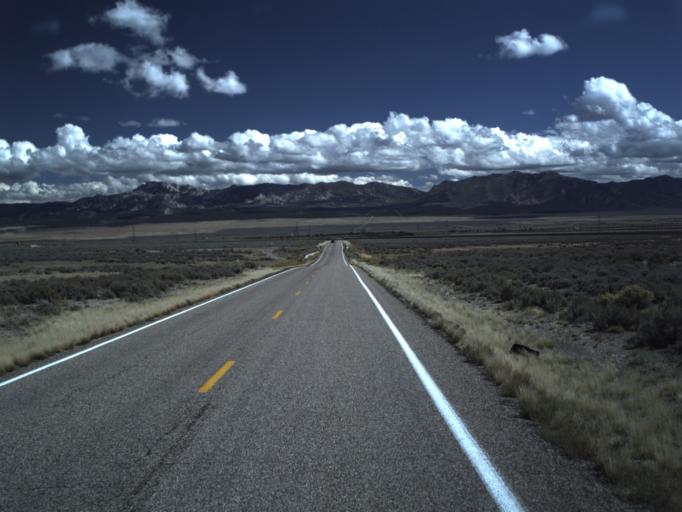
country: US
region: Utah
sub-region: Beaver County
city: Milford
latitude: 38.4175
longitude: -113.0881
